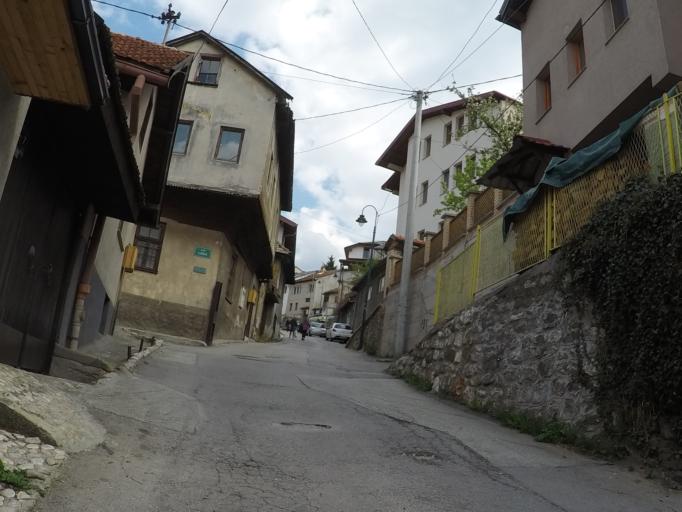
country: BA
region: Federation of Bosnia and Herzegovina
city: Kobilja Glava
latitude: 43.8624
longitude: 18.4380
